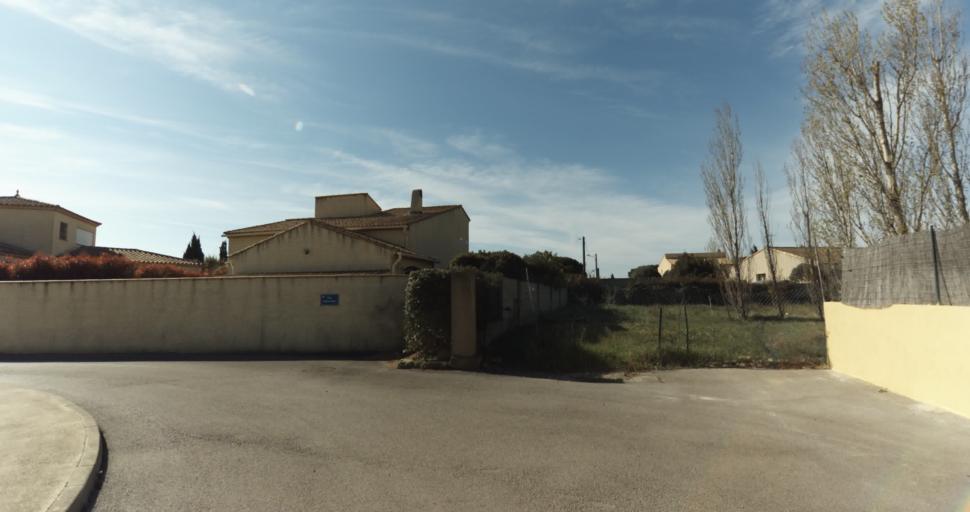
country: FR
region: Languedoc-Roussillon
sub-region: Departement de l'Herault
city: Marseillan
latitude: 43.3374
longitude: 3.5192
